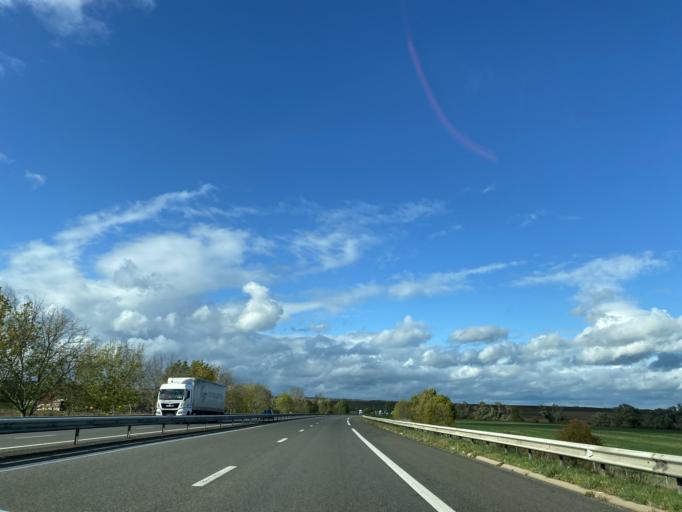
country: FR
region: Auvergne
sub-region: Departement de l'Allier
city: Bellenaves
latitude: 46.1845
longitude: 3.1153
